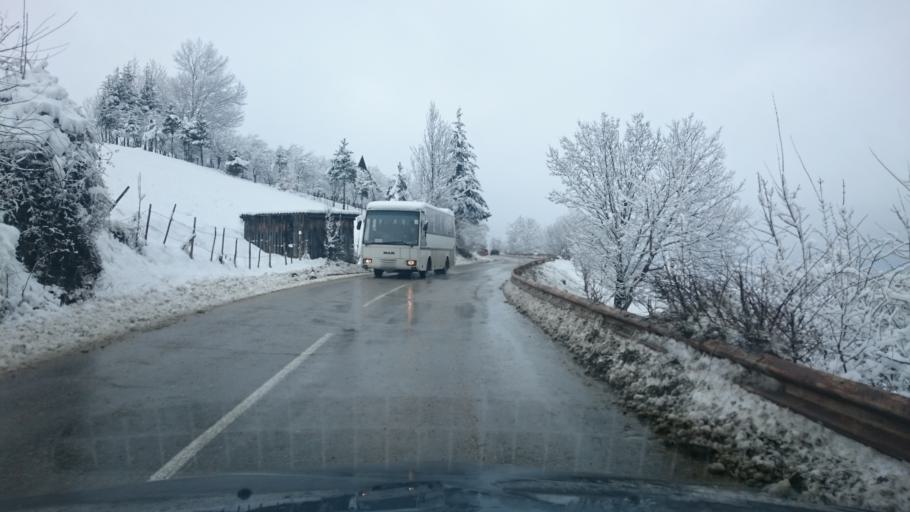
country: BA
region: Republika Srpska
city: Zivinice
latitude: 44.5182
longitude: 17.3005
